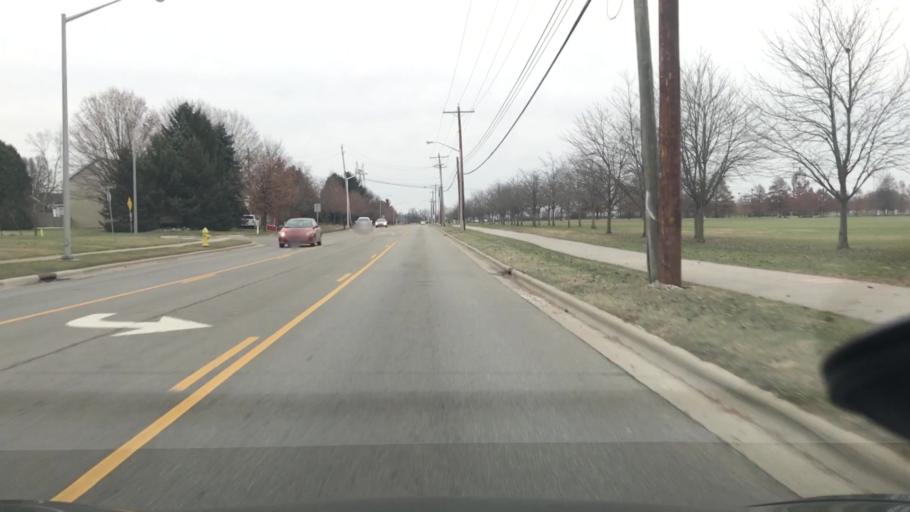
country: US
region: Ohio
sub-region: Franklin County
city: Grove City
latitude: 39.8473
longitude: -83.0720
